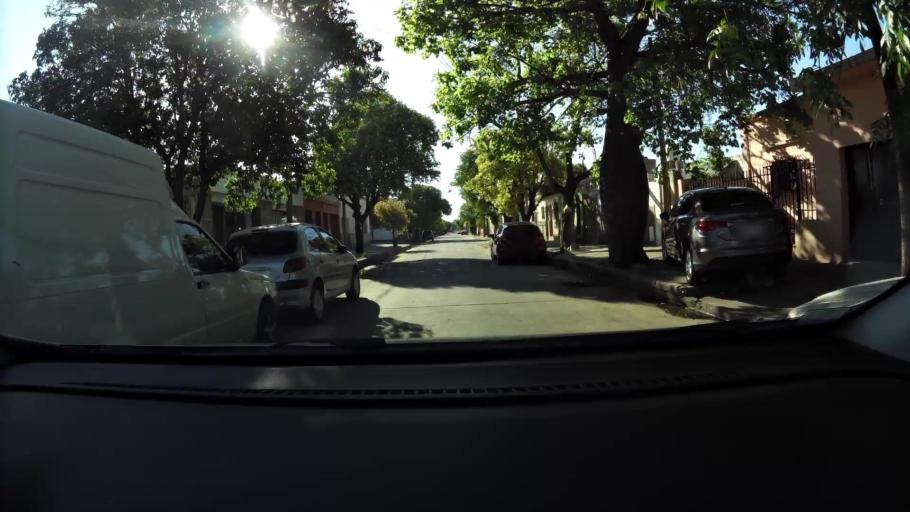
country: AR
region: Cordoba
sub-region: Departamento de Capital
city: Cordoba
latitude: -31.3857
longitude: -64.1722
